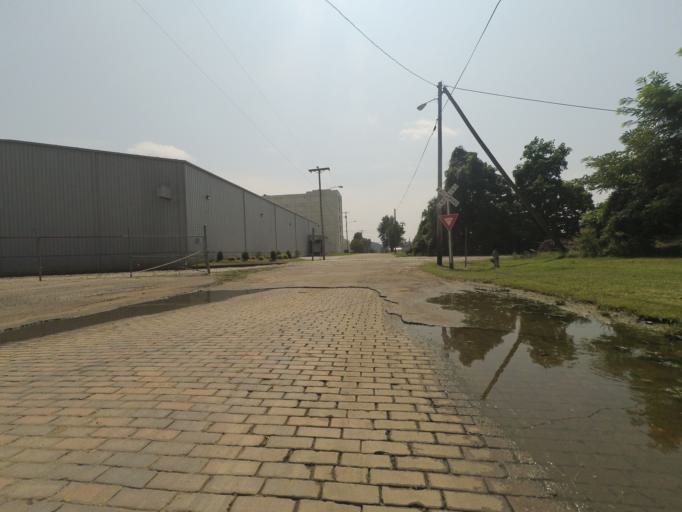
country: US
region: West Virginia
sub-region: Cabell County
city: Huntington
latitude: 38.4318
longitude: -82.4142
